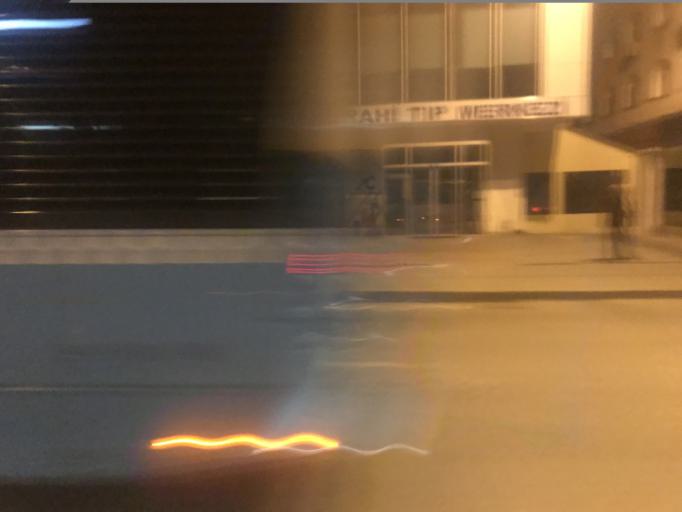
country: TR
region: Istanbul
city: Bahcelievler
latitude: 40.9845
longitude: 28.8723
